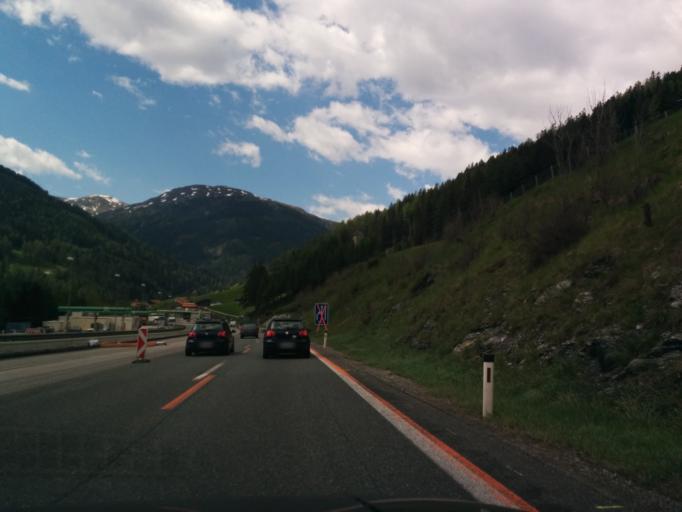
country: AT
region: Tyrol
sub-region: Politischer Bezirk Innsbruck Land
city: Gries am Brenner
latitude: 47.0411
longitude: 11.4760
